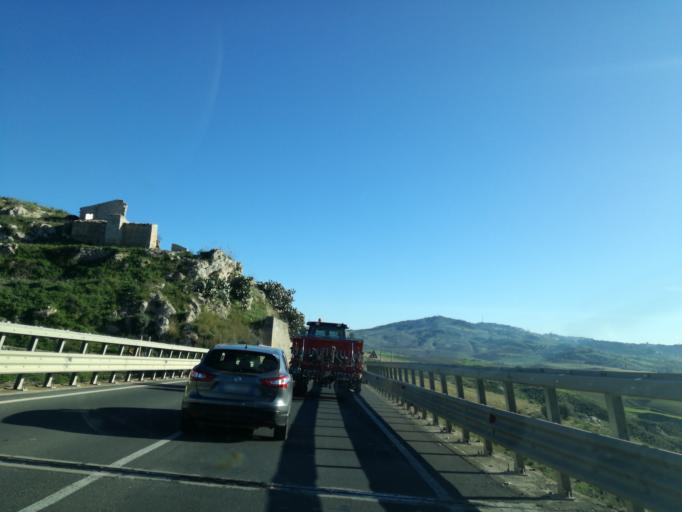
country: IT
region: Sicily
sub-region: Catania
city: San Michele di Ganzaria
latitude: 37.2394
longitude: 14.4515
